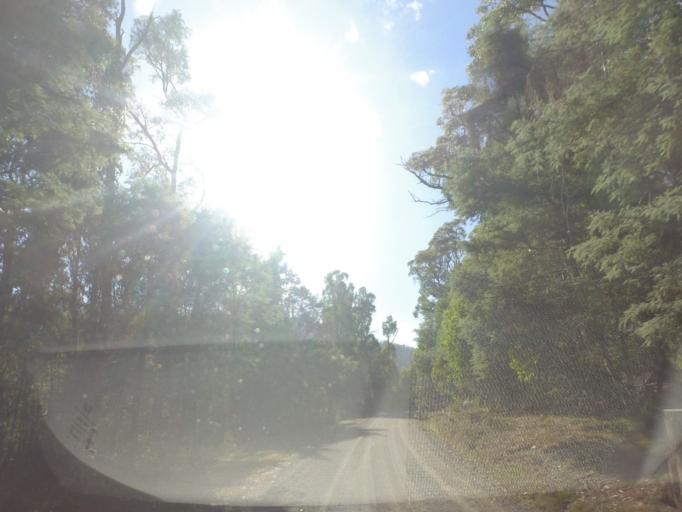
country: AU
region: Victoria
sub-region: Yarra Ranges
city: Millgrove
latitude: -37.5024
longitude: 145.7649
